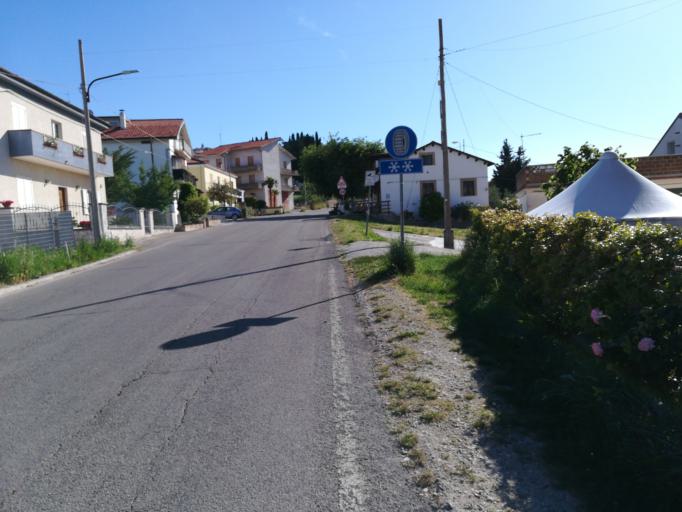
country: IT
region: Abruzzo
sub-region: Provincia di Chieti
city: Bucchianico
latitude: 42.2982
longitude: 14.1746
